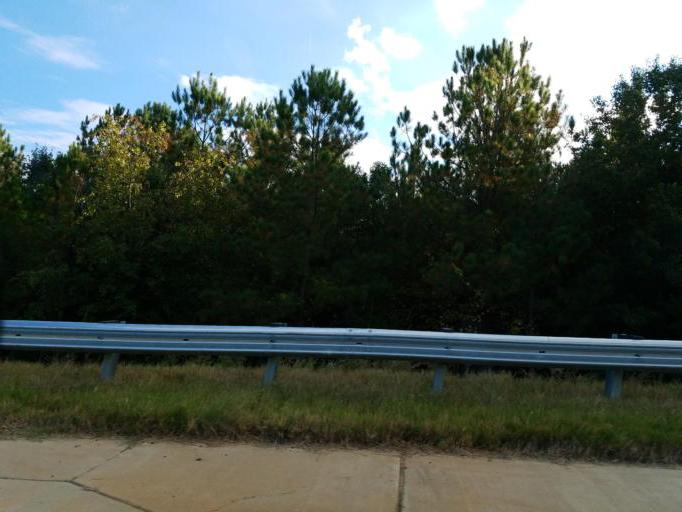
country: US
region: Georgia
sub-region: Bartow County
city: Cartersville
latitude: 34.2070
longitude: -84.7962
